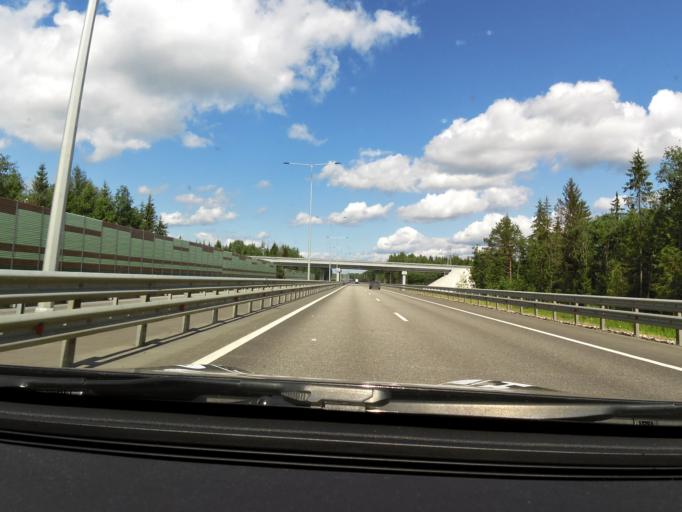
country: RU
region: Tverskaya
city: Vydropuzhsk
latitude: 57.3153
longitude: 34.7574
